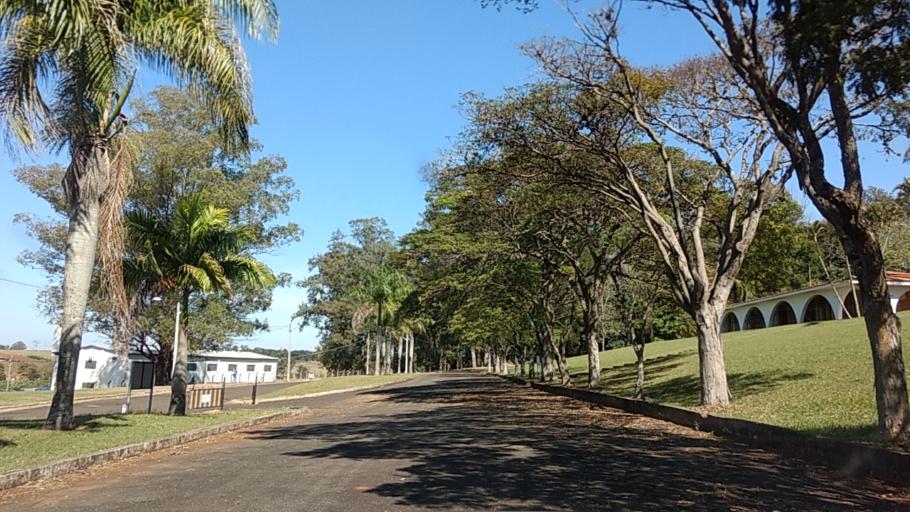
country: BR
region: Sao Paulo
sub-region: Botucatu
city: Botucatu
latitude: -22.8519
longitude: -48.4316
